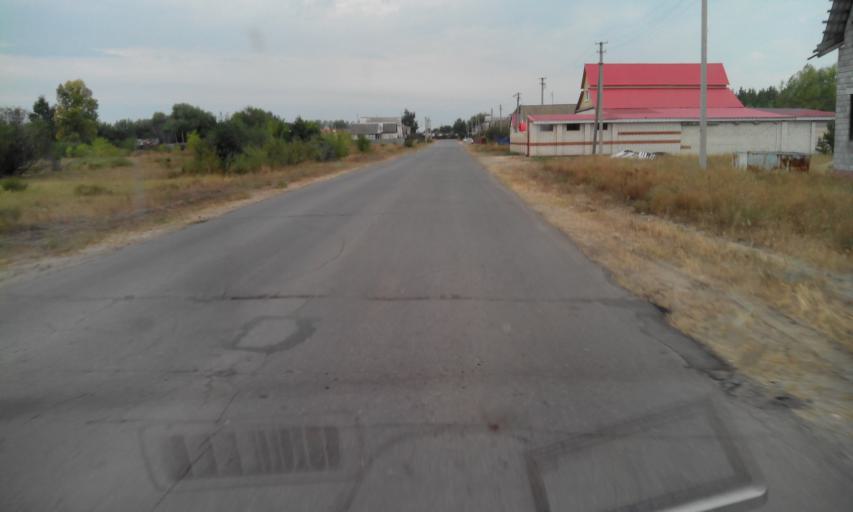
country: RU
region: Samara
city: Balasheyka
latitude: 53.1546
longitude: 48.1195
